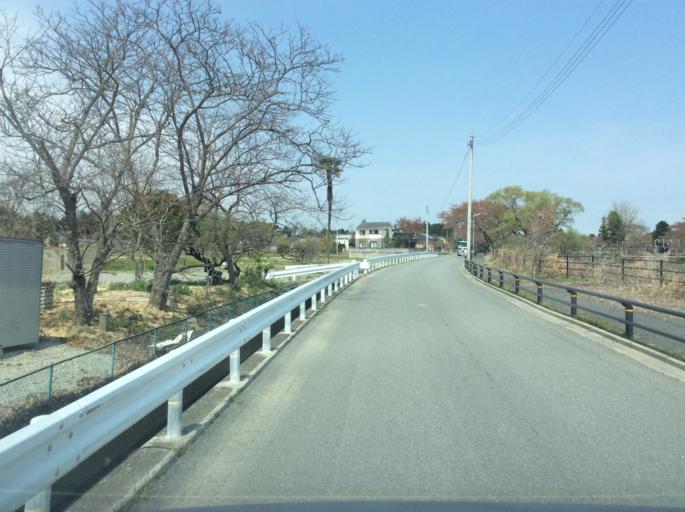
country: JP
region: Fukushima
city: Namie
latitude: 37.3631
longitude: 140.9919
